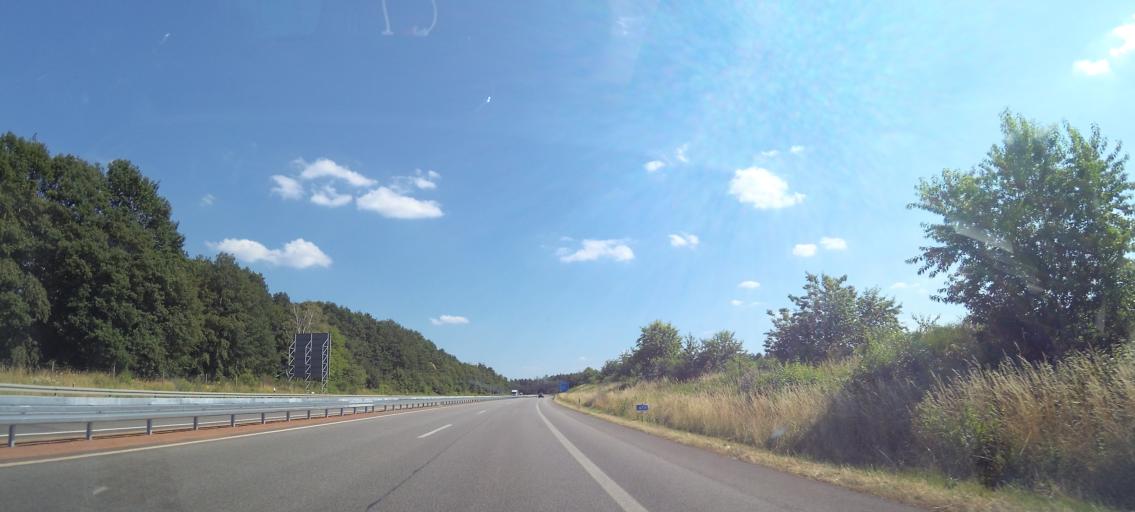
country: DE
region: Saarland
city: Saarwellingen
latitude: 49.3379
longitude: 6.8030
